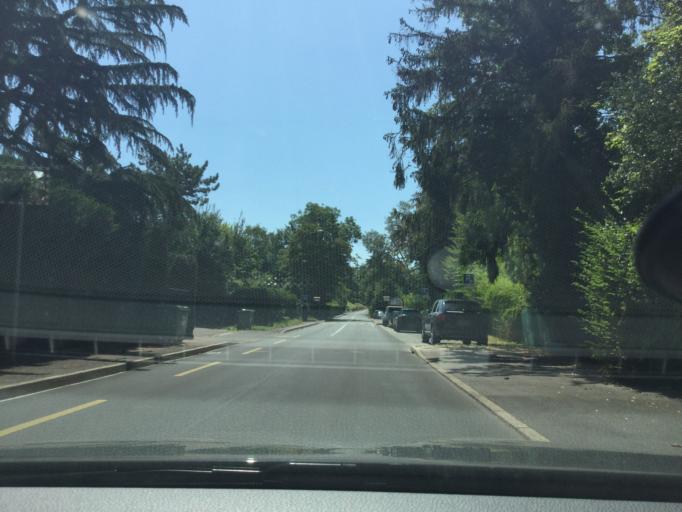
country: CH
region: Geneva
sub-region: Geneva
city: Anieres
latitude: 46.2837
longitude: 6.2297
